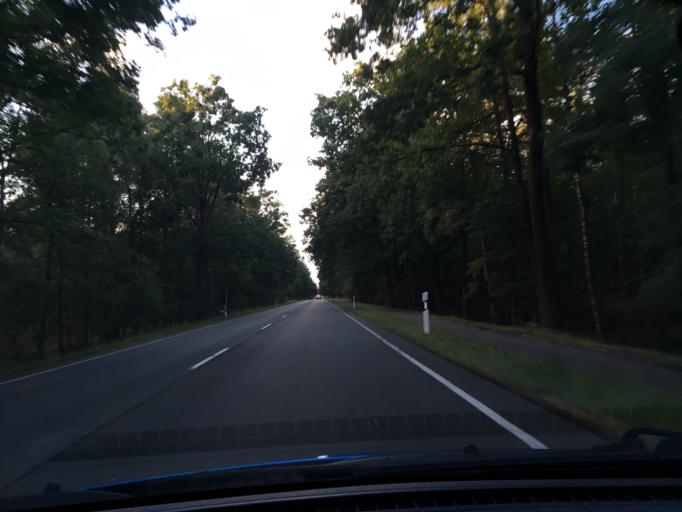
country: DE
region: Lower Saxony
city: Bergen
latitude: 52.7568
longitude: 9.9784
